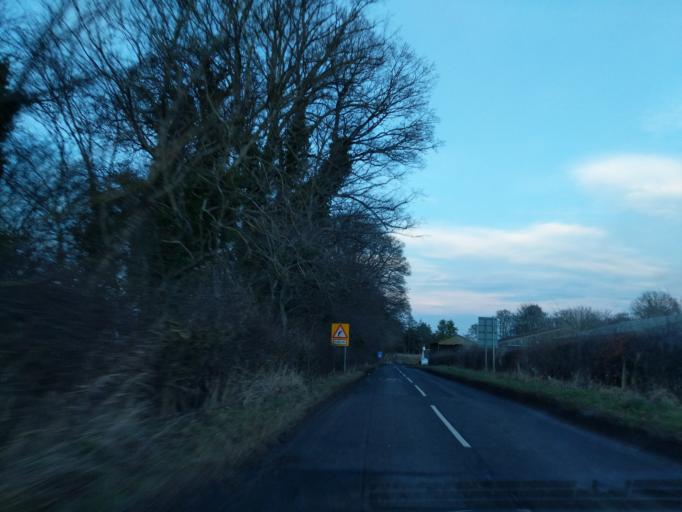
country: GB
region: Scotland
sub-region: Midlothian
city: Bonnyrigg
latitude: 55.8159
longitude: -3.1018
